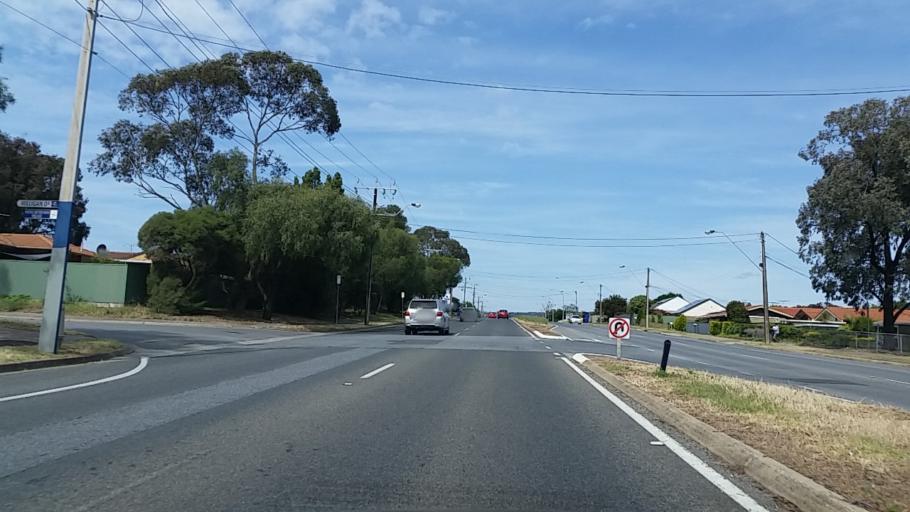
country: AU
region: South Australia
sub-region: Tea Tree Gully
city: Modbury
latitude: -34.8294
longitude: 138.6651
